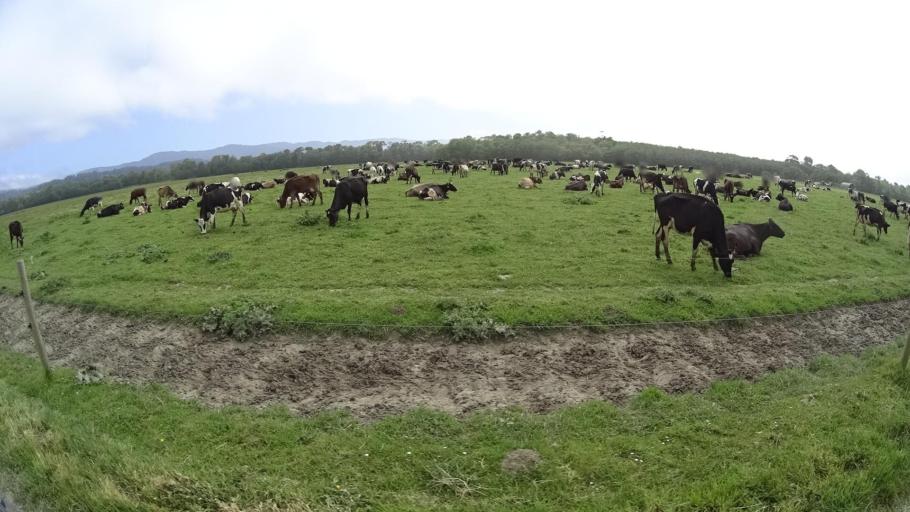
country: US
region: California
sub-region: Humboldt County
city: Fortuna
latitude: 40.5880
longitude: -124.1879
